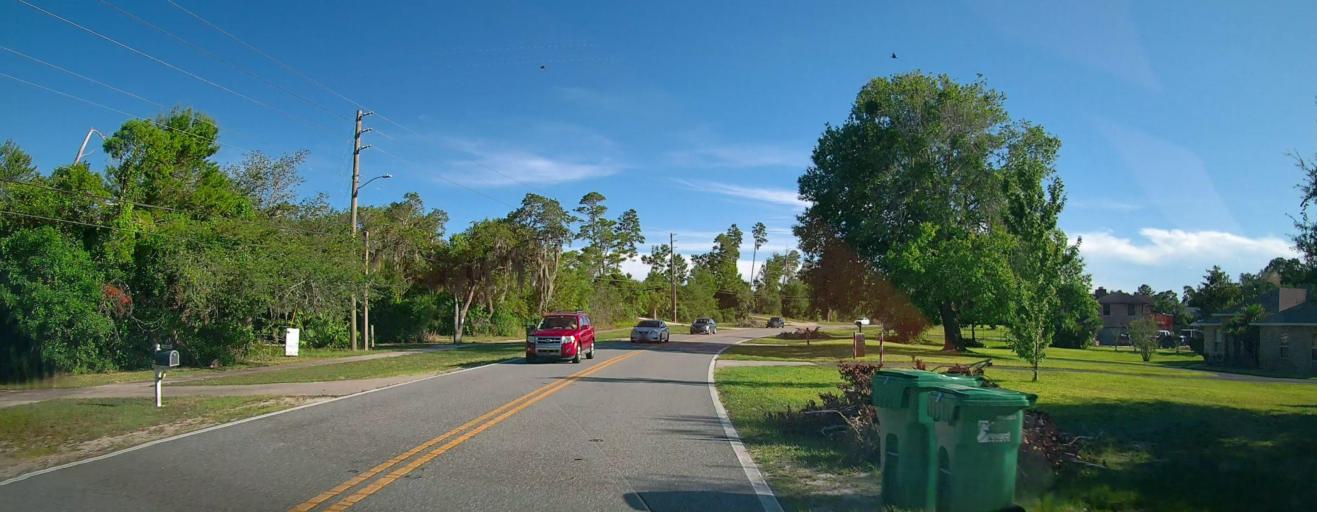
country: US
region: Florida
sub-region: Brevard County
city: Port Saint John
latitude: 28.5405
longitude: -80.8216
